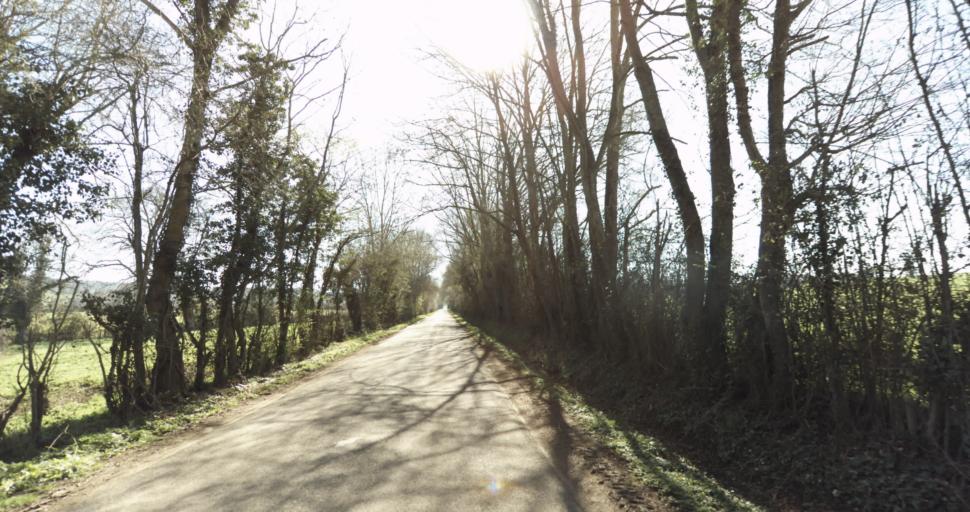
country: FR
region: Lower Normandy
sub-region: Departement du Calvados
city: Saint-Pierre-sur-Dives
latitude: 48.9707
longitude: 0.0478
